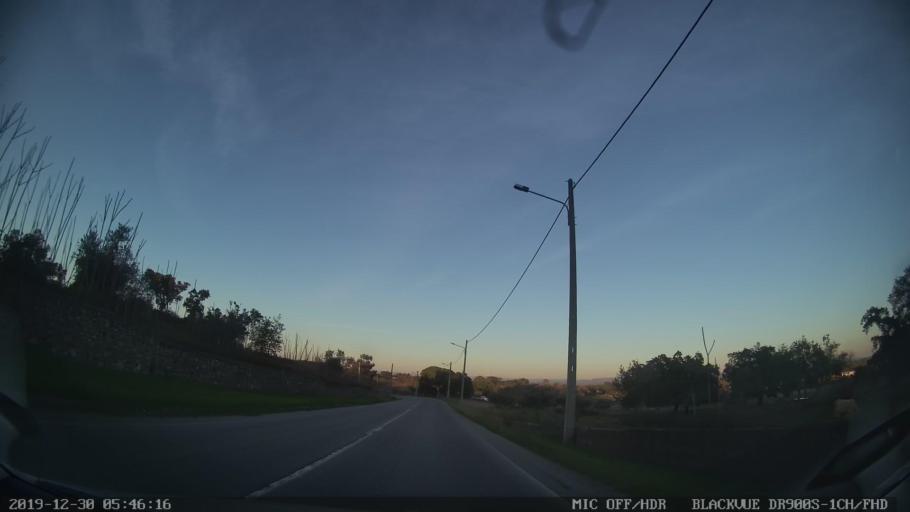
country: PT
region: Castelo Branco
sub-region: Idanha-A-Nova
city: Idanha-a-Nova
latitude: 39.9411
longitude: -7.2363
